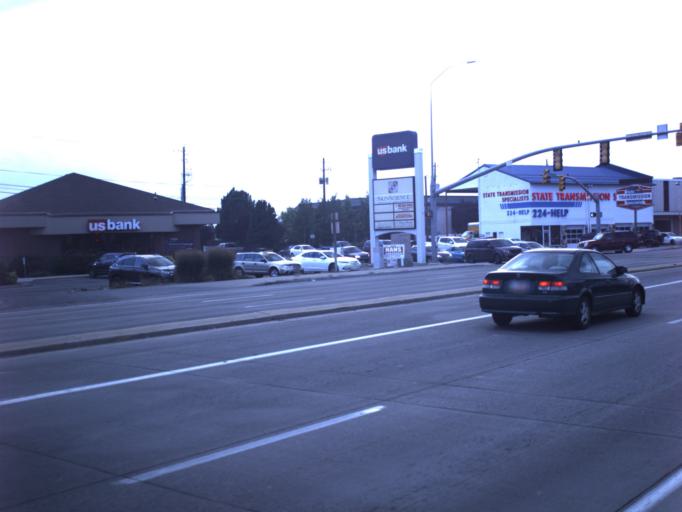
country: US
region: Utah
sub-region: Utah County
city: Orem
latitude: 40.2747
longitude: -111.6850
